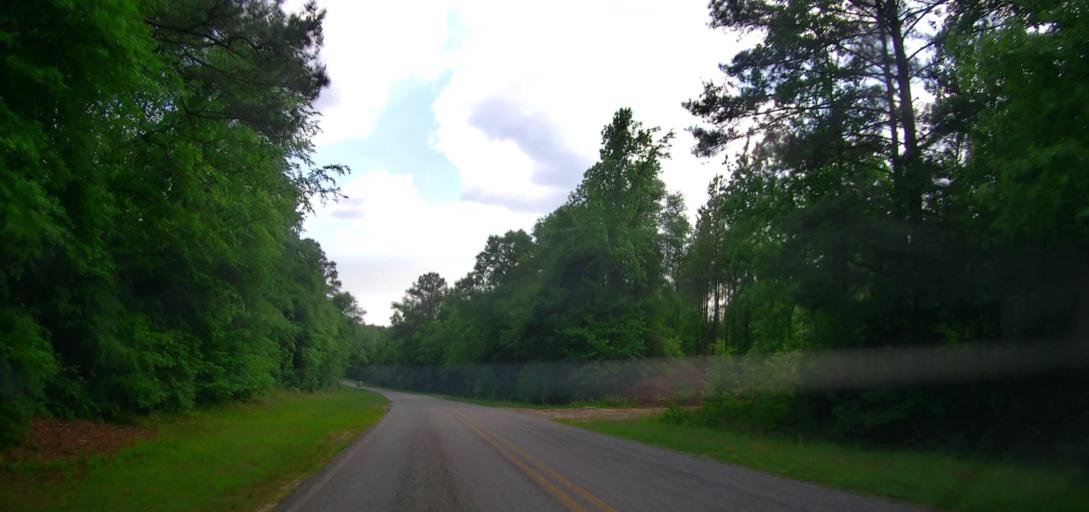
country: US
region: Georgia
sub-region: Laurens County
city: East Dublin
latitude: 32.6736
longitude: -82.8955
